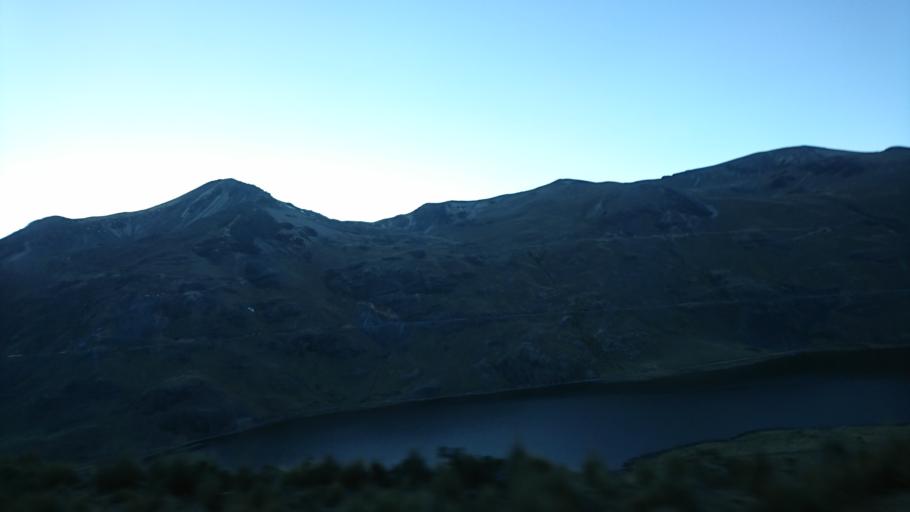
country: BO
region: La Paz
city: La Paz
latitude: -16.3914
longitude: -68.0439
